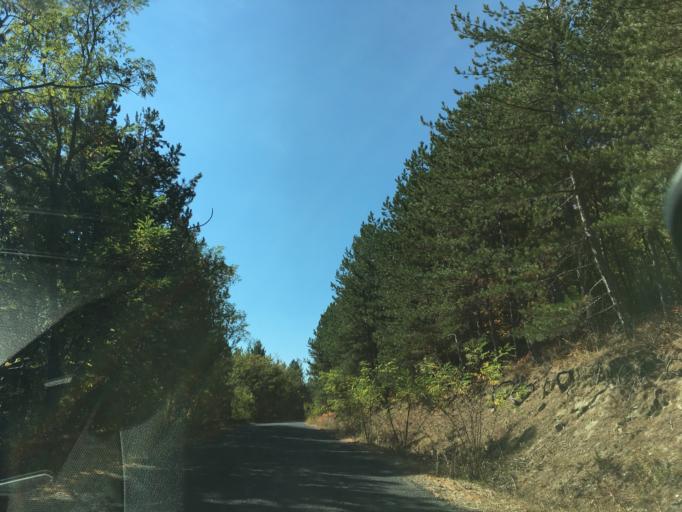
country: BG
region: Kurdzhali
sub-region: Obshtina Krumovgrad
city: Krumovgrad
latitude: 41.5509
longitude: 25.5564
